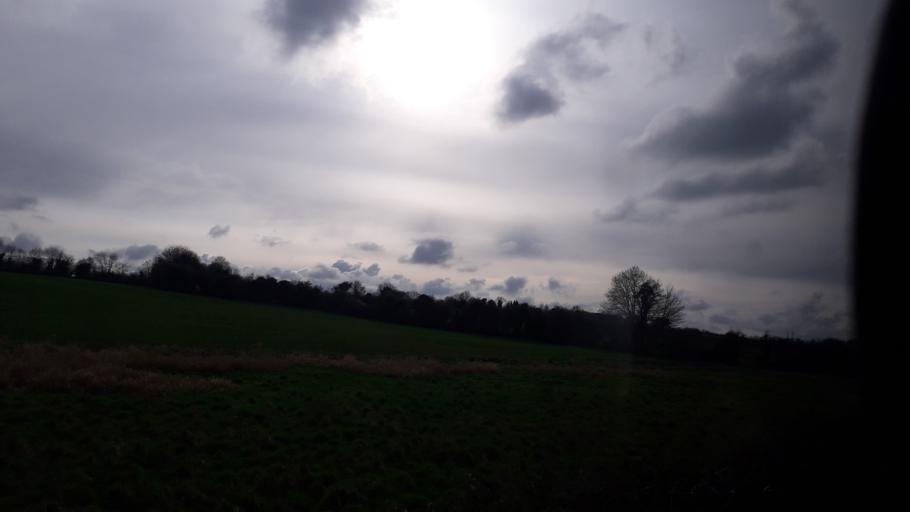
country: IE
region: Leinster
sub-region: Kildare
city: Kilcock
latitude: 53.4174
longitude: -6.7034
